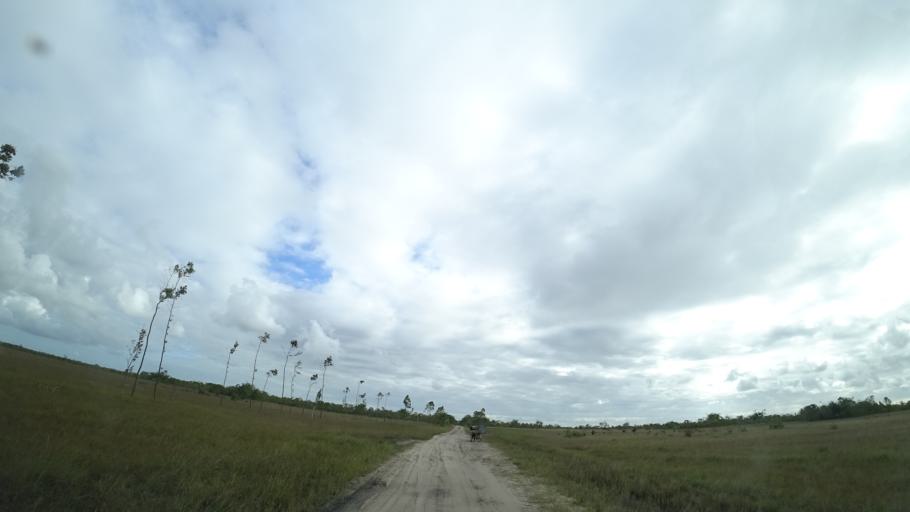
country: MZ
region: Sofala
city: Beira
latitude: -19.6114
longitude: 35.0793
